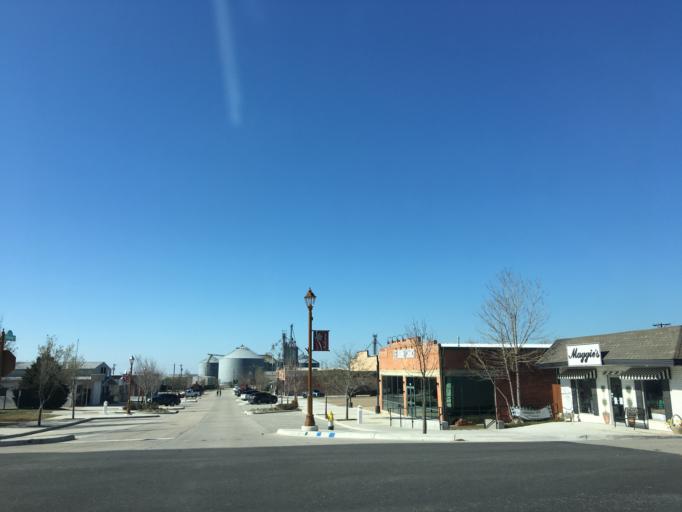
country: US
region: Texas
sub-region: Collin County
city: Prosper
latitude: 33.2369
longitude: -96.8018
